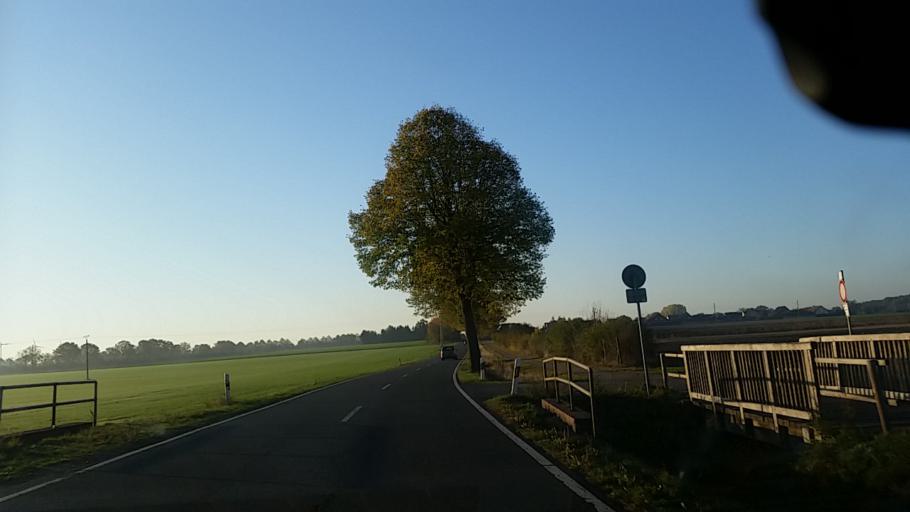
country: DE
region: Lower Saxony
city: Jembke
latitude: 52.4837
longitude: 10.7714
